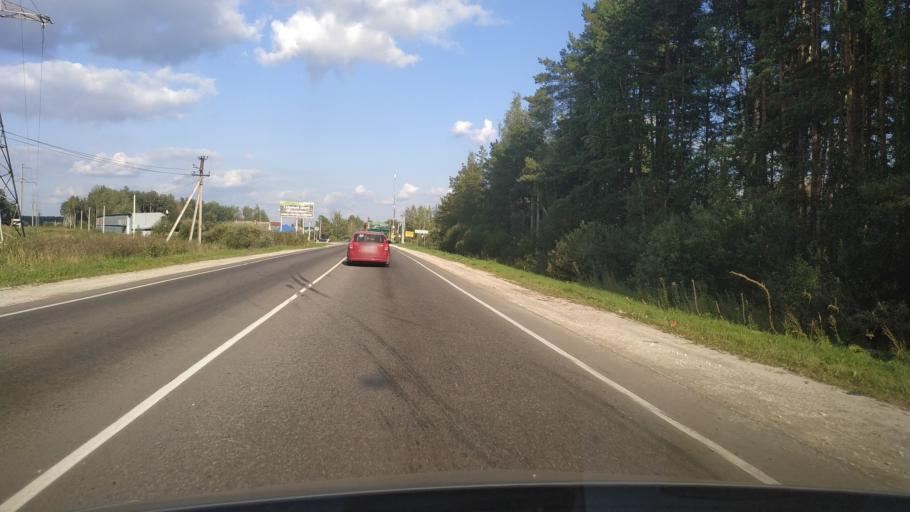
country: RU
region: Moskovskaya
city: Shaturtorf
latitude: 55.5792
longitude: 39.4590
